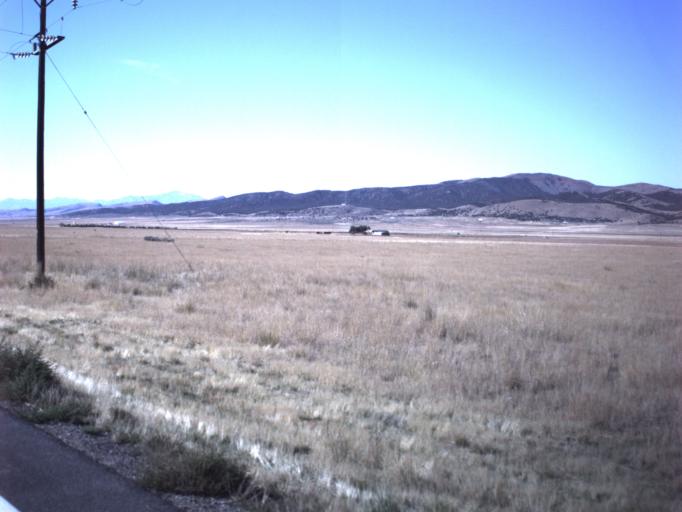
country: US
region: Utah
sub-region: Juab County
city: Nephi
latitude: 39.6514
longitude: -111.8586
